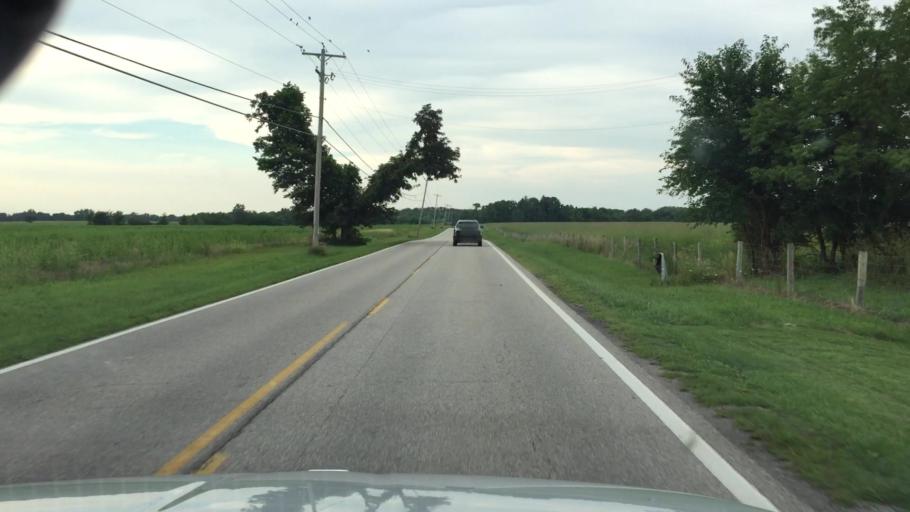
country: US
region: Ohio
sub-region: Madison County
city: West Jefferson
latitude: 39.9889
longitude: -83.2642
